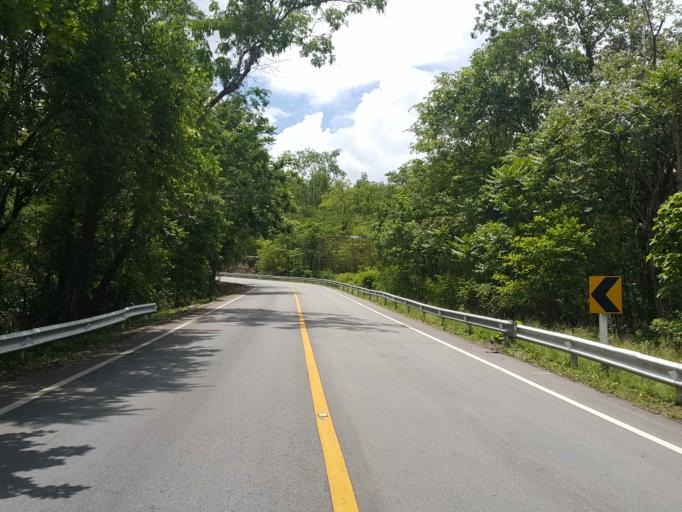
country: TH
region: Chiang Mai
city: Chom Thong
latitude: 18.4996
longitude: 98.6717
